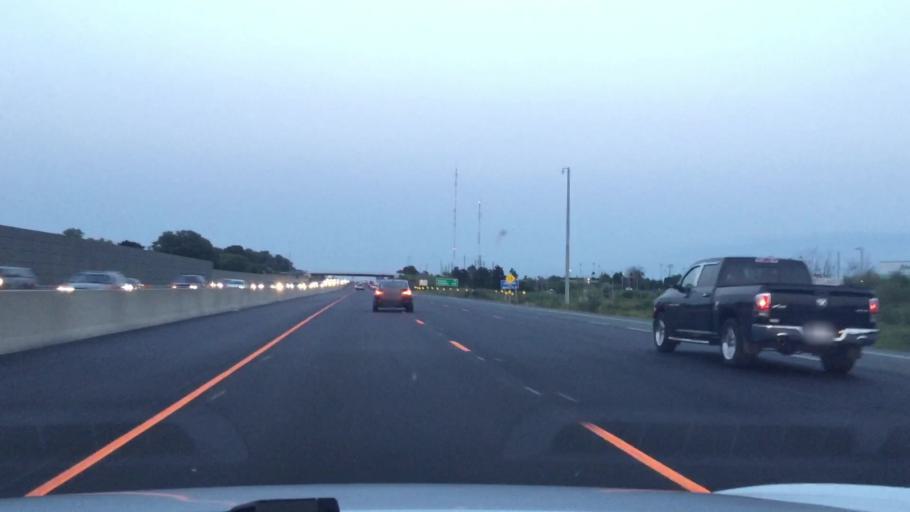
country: CA
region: Ontario
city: Ajax
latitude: 43.8668
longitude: -78.9517
